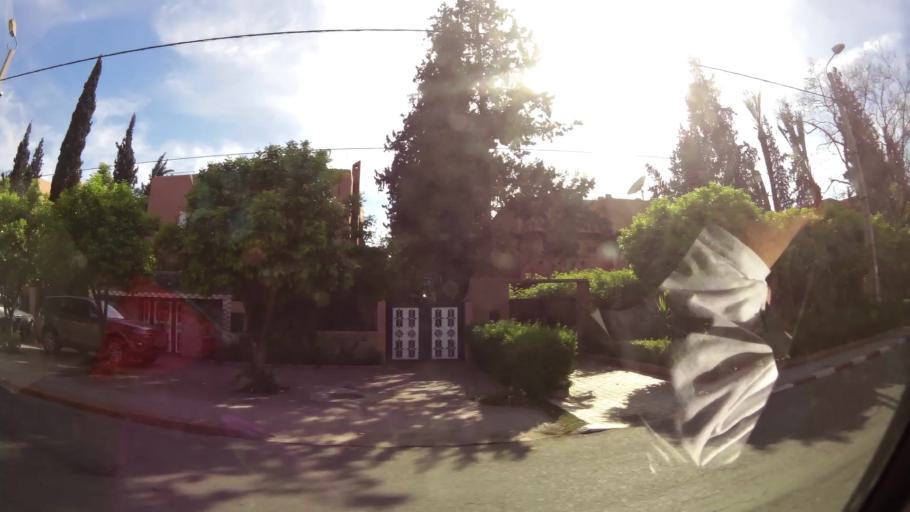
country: MA
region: Marrakech-Tensift-Al Haouz
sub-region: Marrakech
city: Marrakesh
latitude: 31.6544
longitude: -8.0095
